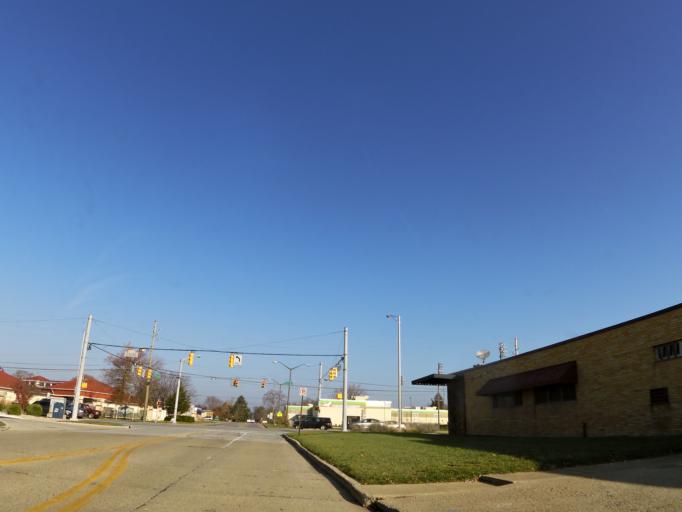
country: US
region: Indiana
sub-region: Marion County
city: Indianapolis
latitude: 39.7887
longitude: -86.1910
